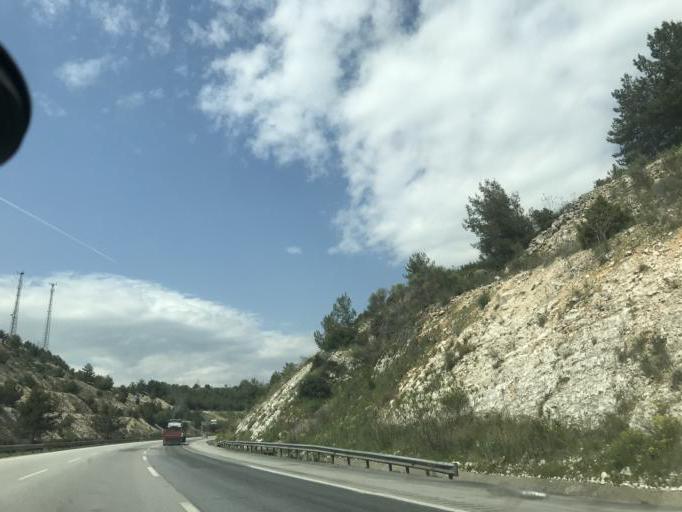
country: TR
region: Mersin
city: Tarsus
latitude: 37.1530
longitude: 34.8395
